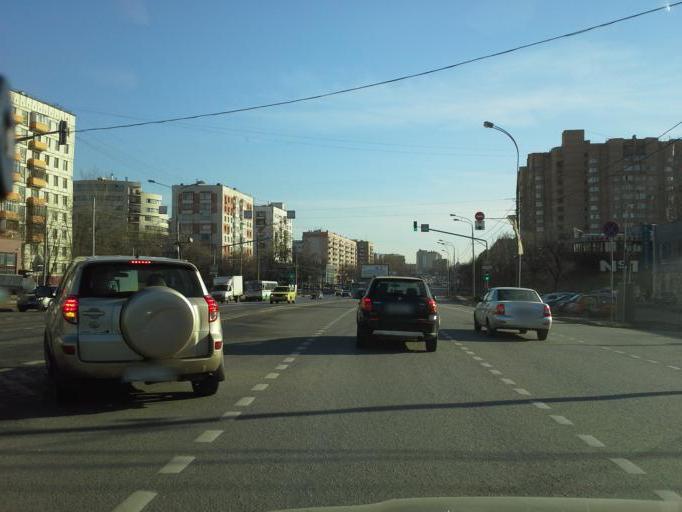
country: RU
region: Moscow
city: Taganskiy
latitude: 55.7254
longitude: 37.6635
